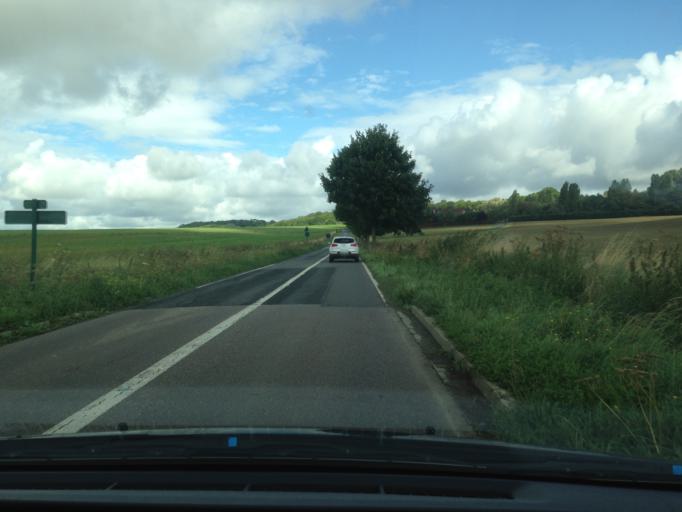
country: FR
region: Ile-de-France
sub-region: Departement du Val-d'Oise
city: Osny
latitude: 49.1221
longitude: 2.0501
